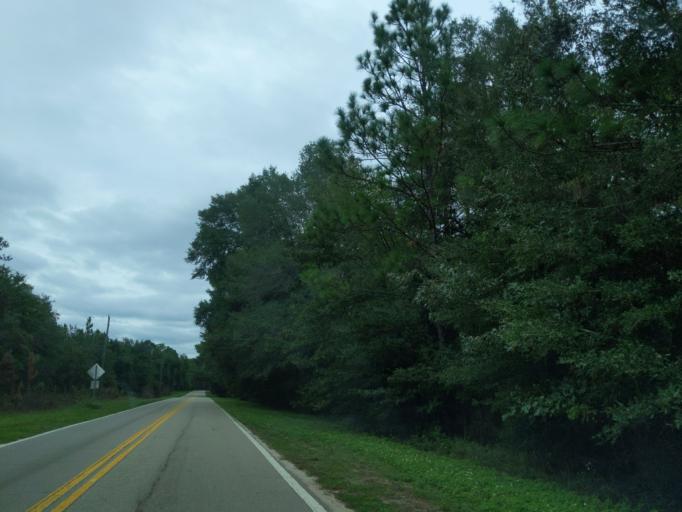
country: US
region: Florida
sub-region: Gadsden County
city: Midway
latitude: 30.4257
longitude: -84.4127
